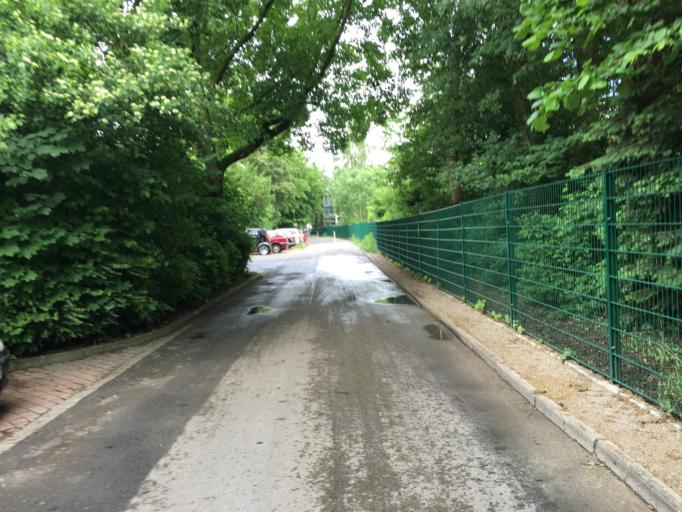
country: DE
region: North Rhine-Westphalia
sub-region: Regierungsbezirk Munster
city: Muenster
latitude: 51.9598
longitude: 7.6523
